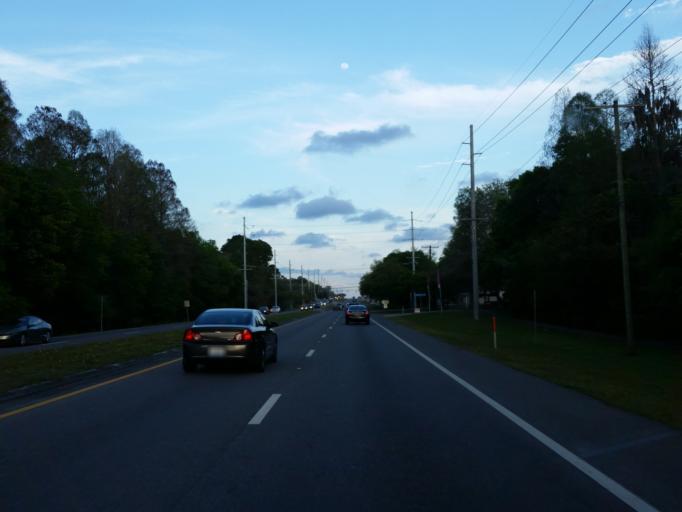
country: US
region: Florida
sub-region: Hillsborough County
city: Temple Terrace
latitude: 28.0692
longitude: -82.3993
